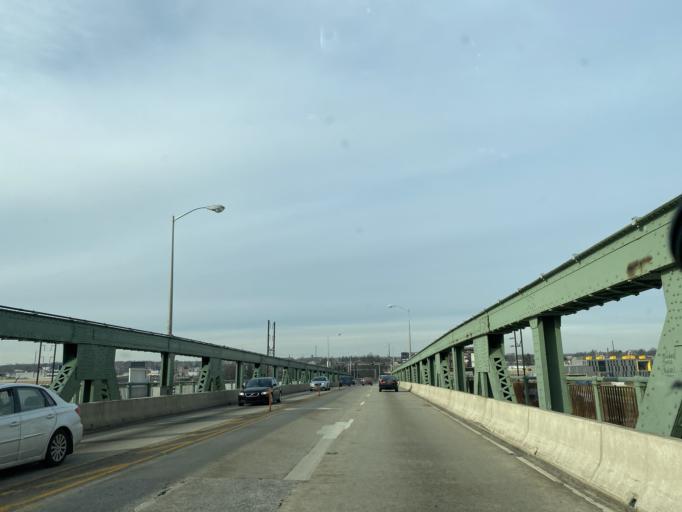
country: US
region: New Jersey
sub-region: Burlington County
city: Palmyra
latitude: 40.0138
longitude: -75.0441
